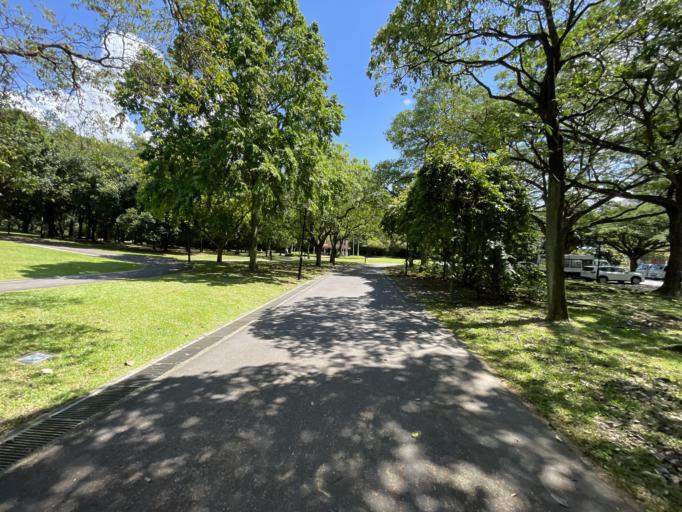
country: SG
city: Singapore
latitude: 1.2990
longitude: 103.7626
